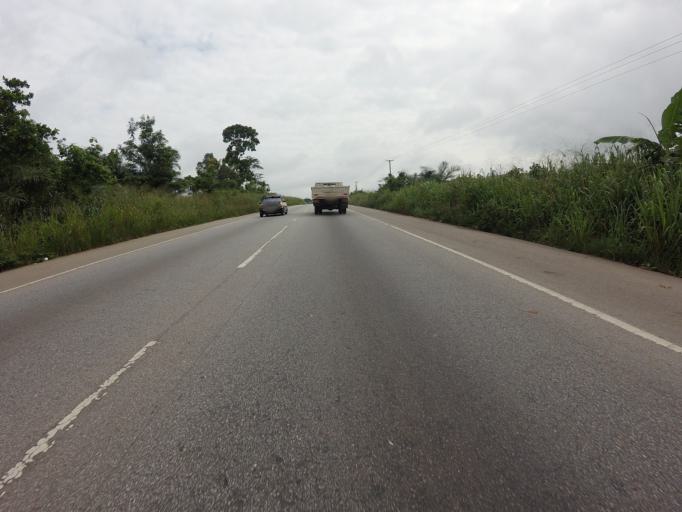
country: GH
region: Ashanti
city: Tafo
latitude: 6.9788
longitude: -1.6868
